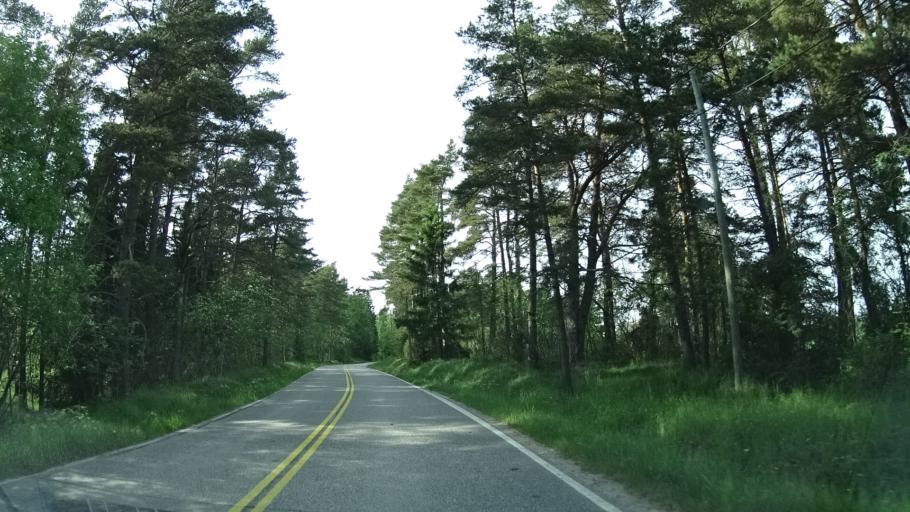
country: FI
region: Uusimaa
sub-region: Helsinki
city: Kirkkonummi
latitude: 60.0939
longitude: 24.5020
